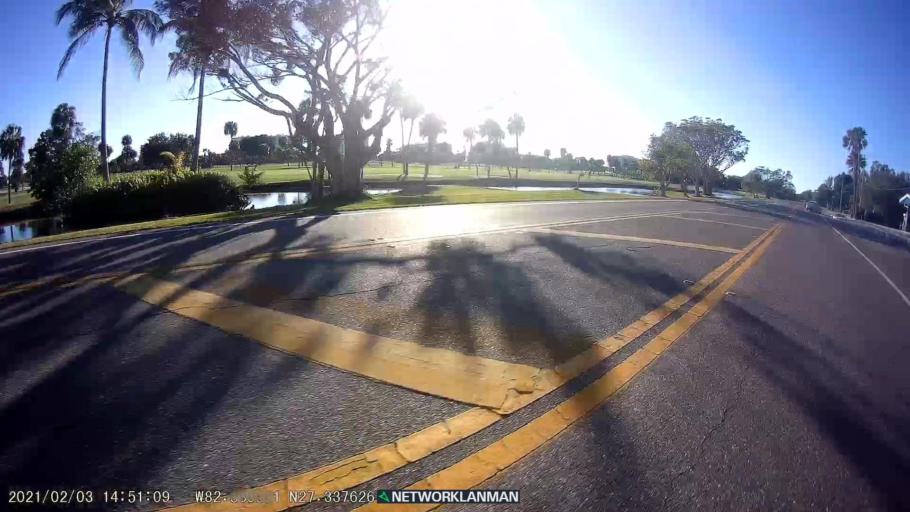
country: US
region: Florida
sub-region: Sarasota County
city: Siesta Key
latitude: 27.3373
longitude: -82.5898
